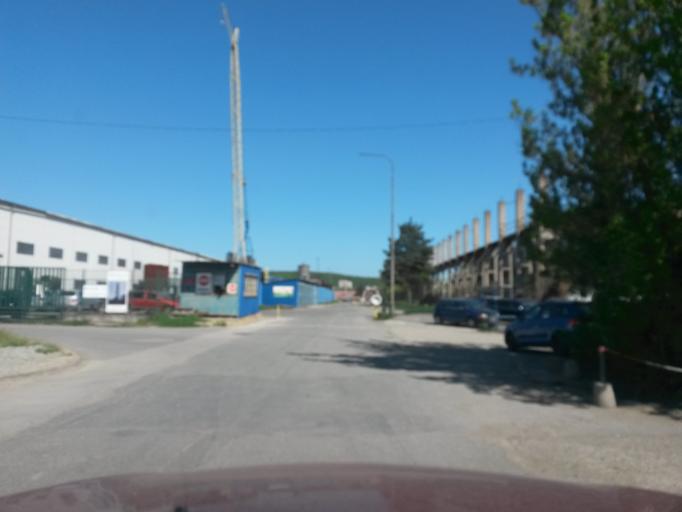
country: SK
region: Kosicky
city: Kosice
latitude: 48.6819
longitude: 21.2720
